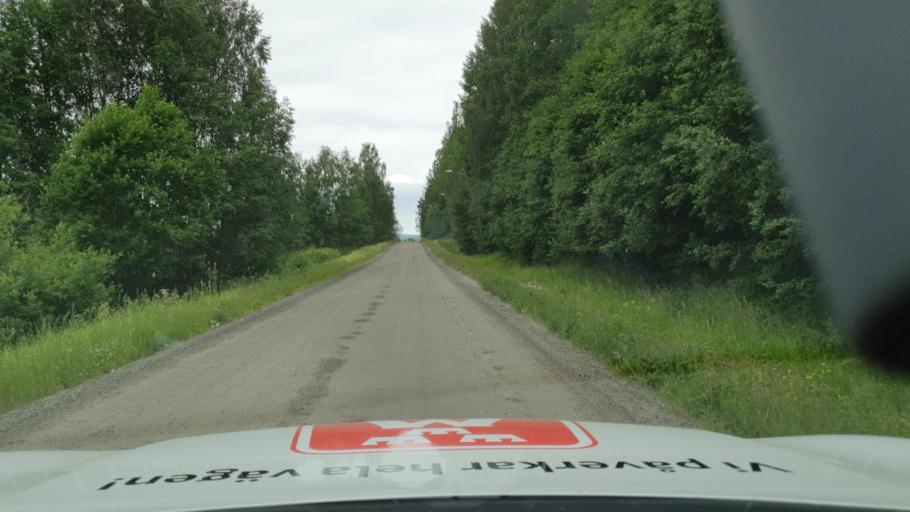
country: SE
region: Vaesterbotten
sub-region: Bjurholms Kommun
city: Bjurholm
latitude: 63.7795
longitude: 19.3899
